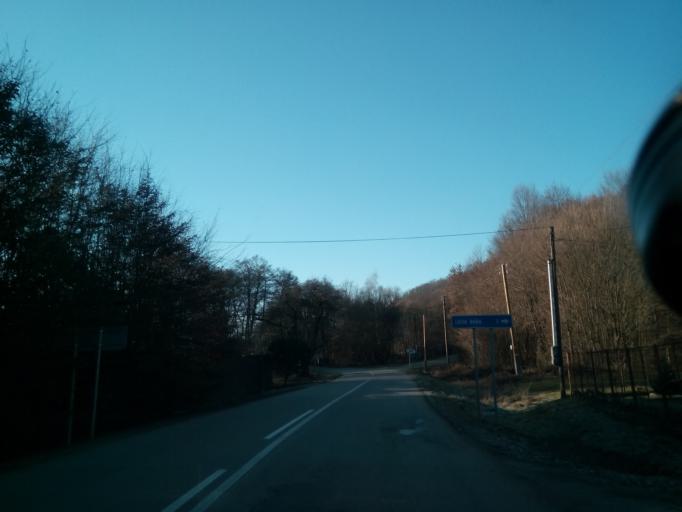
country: SK
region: Kosicky
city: Medzev
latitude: 48.6945
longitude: 20.9373
